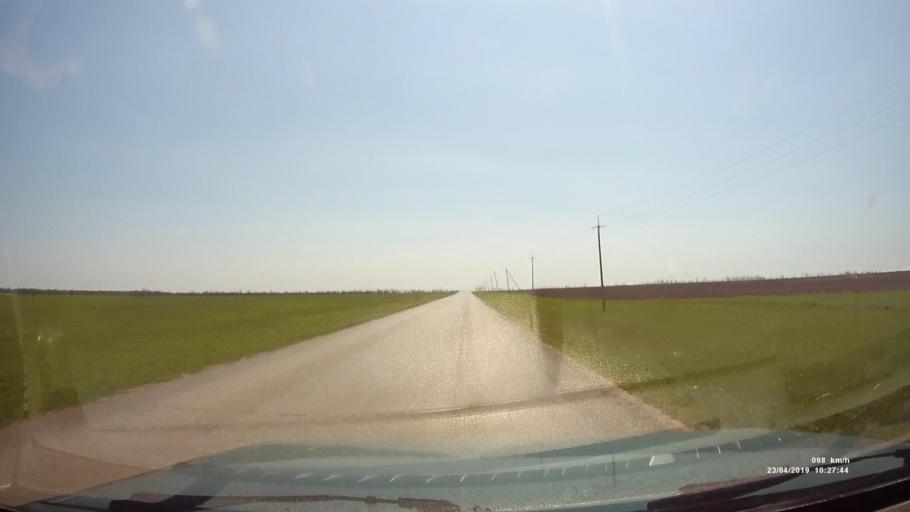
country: RU
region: Kalmykiya
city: Yashalta
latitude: 46.6112
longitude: 42.4960
